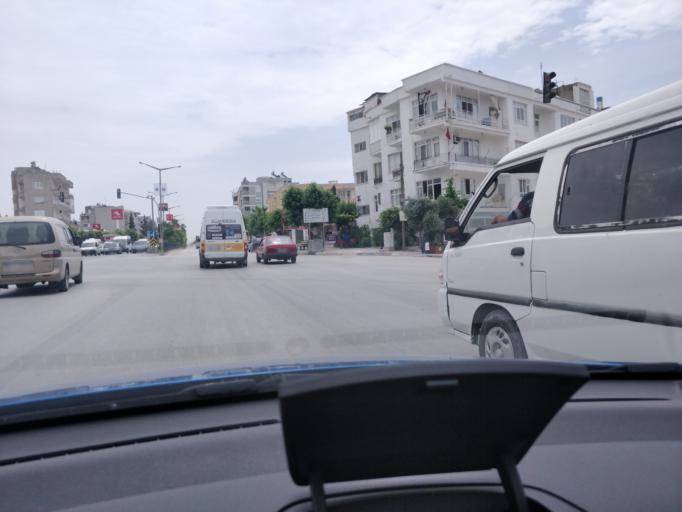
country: TR
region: Mersin
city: Mut
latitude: 36.6422
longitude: 33.4404
